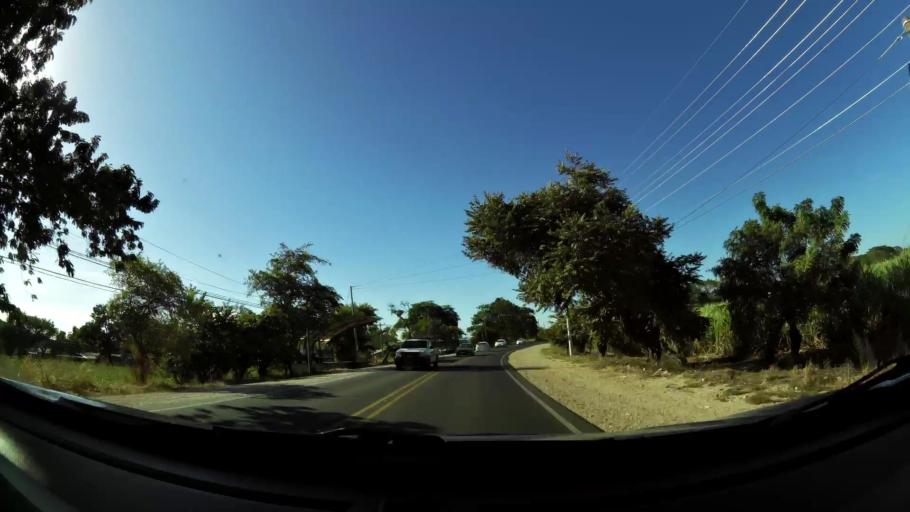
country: CR
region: Guanacaste
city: Belen
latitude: 10.4403
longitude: -85.5567
